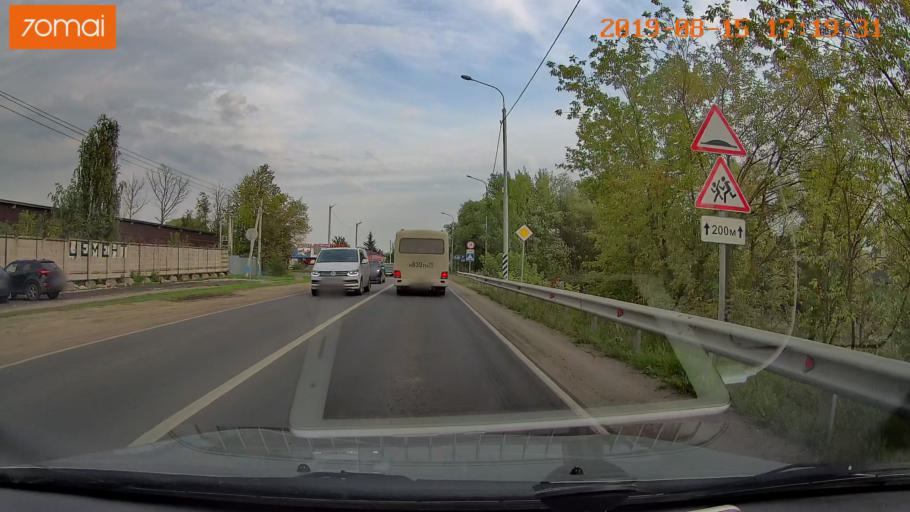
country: RU
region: Moskovskaya
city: Ashitkovo
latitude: 55.4262
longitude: 38.5539
